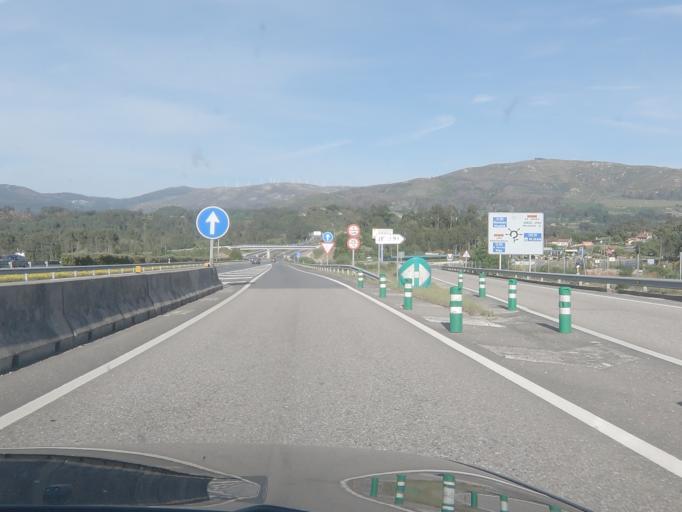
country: ES
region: Galicia
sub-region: Provincia de Pontevedra
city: Ponteareas
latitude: 42.1425
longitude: -8.4668
